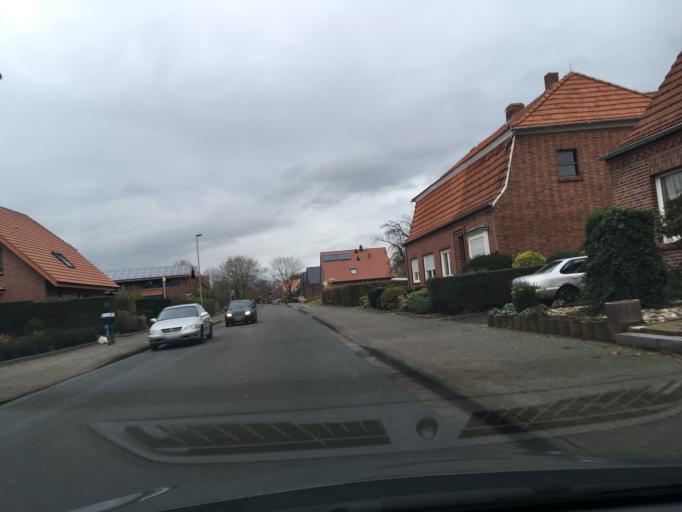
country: DE
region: North Rhine-Westphalia
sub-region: Regierungsbezirk Munster
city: Ahaus
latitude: 52.0966
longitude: 6.9792
